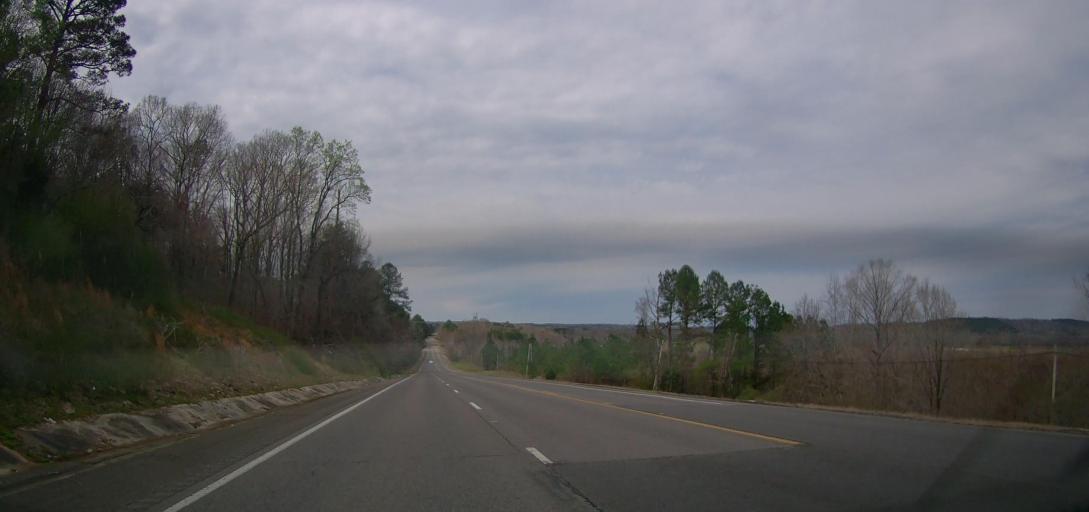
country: US
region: Alabama
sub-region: Marion County
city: Hamilton
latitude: 34.0877
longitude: -87.9811
